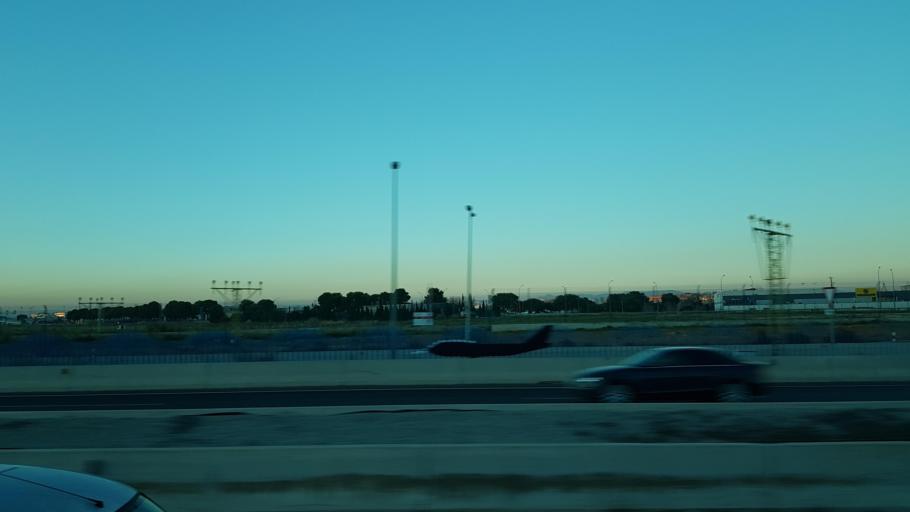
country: ES
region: Valencia
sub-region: Provincia de Valencia
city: Manises
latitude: 39.4811
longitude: -0.4610
